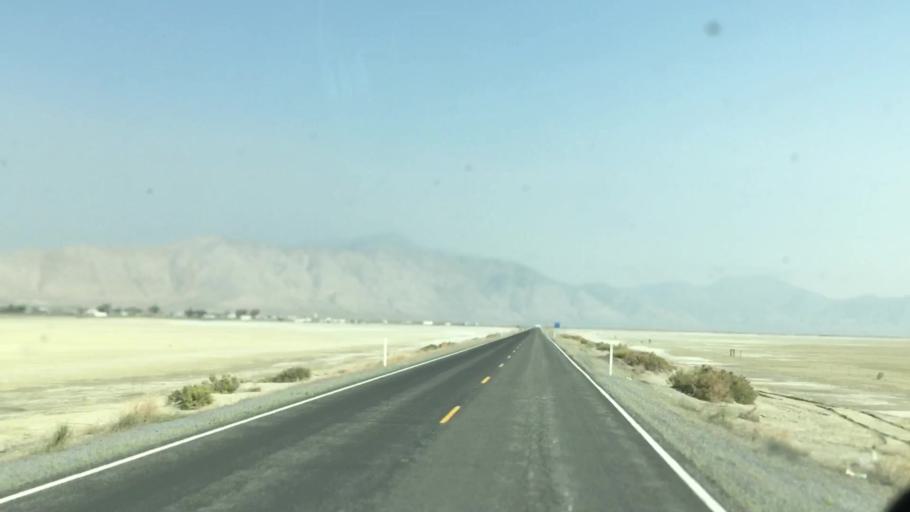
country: US
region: Nevada
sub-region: Pershing County
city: Lovelock
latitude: 40.6405
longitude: -119.3410
